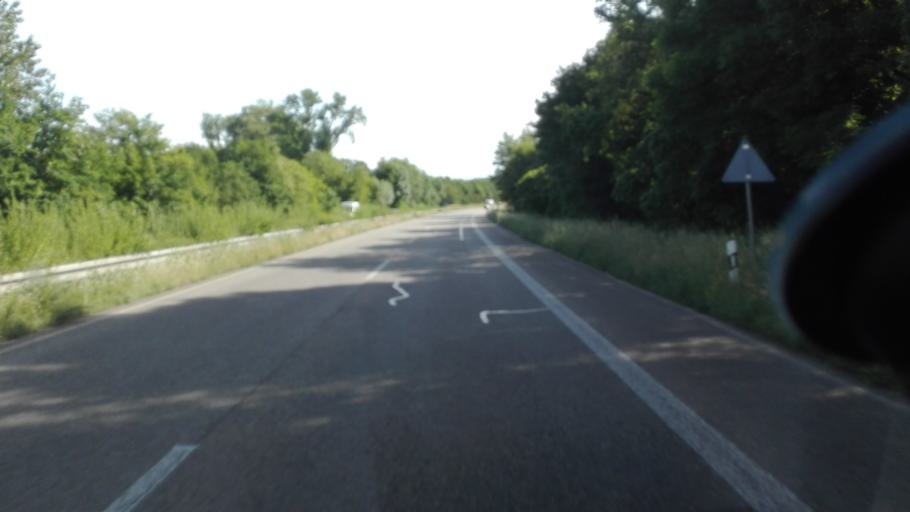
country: DE
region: Baden-Wuerttemberg
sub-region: Karlsruhe Region
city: Eggenstein-Leopoldshafen
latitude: 49.0580
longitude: 8.3715
